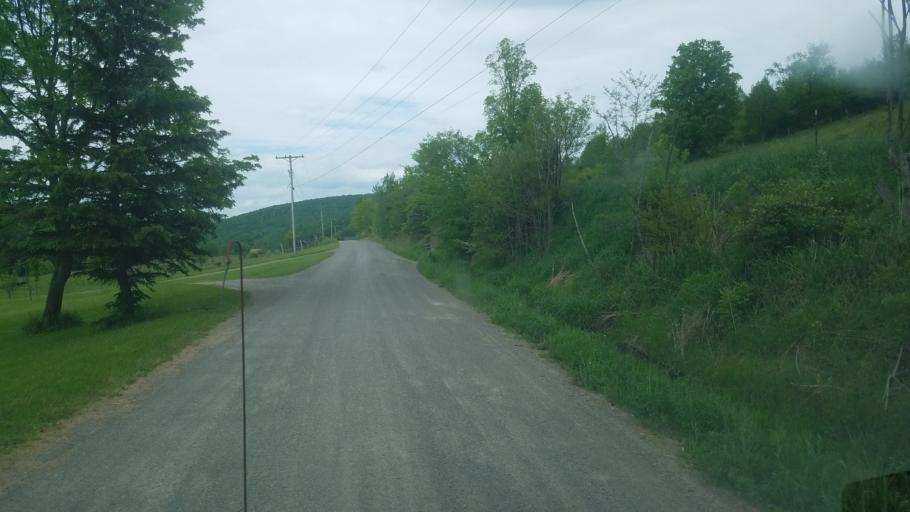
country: US
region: Pennsylvania
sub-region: Tioga County
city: Westfield
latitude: 41.8738
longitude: -77.5961
